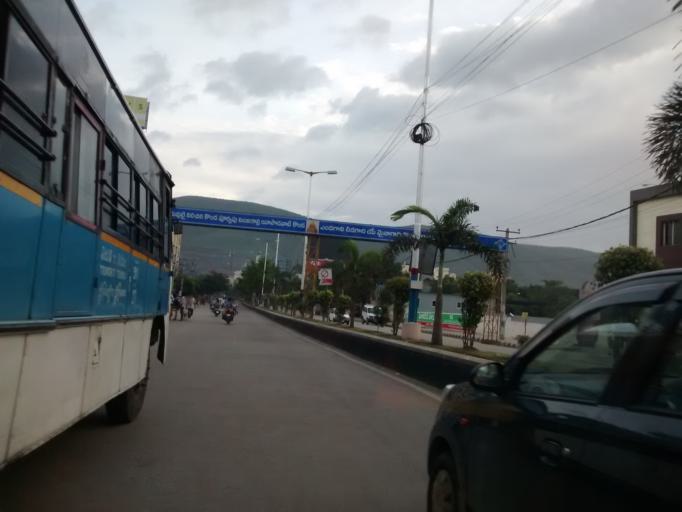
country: IN
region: Andhra Pradesh
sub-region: Chittoor
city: Tirupati
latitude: 13.6423
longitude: 79.4276
